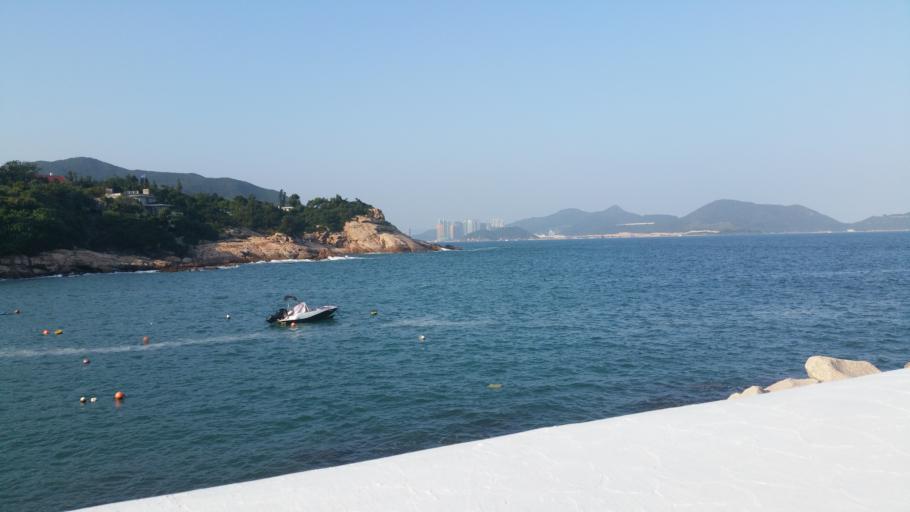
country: HK
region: Wanchai
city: Wan Chai
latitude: 22.2310
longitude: 114.2528
